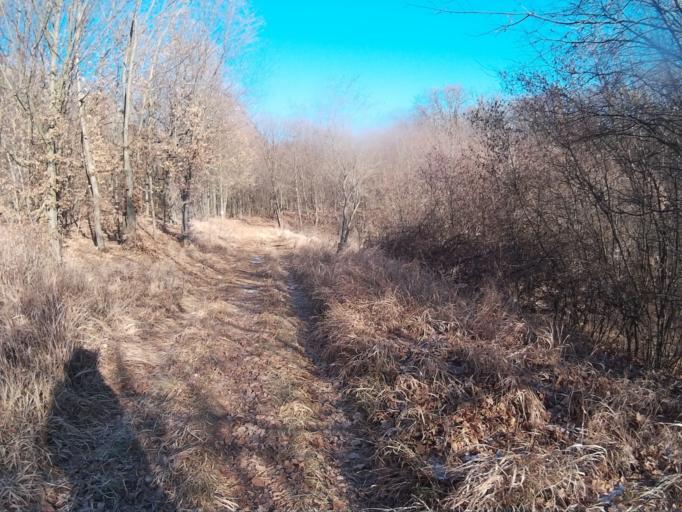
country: HU
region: Borsod-Abauj-Zemplen
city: Rudabanya
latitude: 48.4926
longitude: 20.5846
